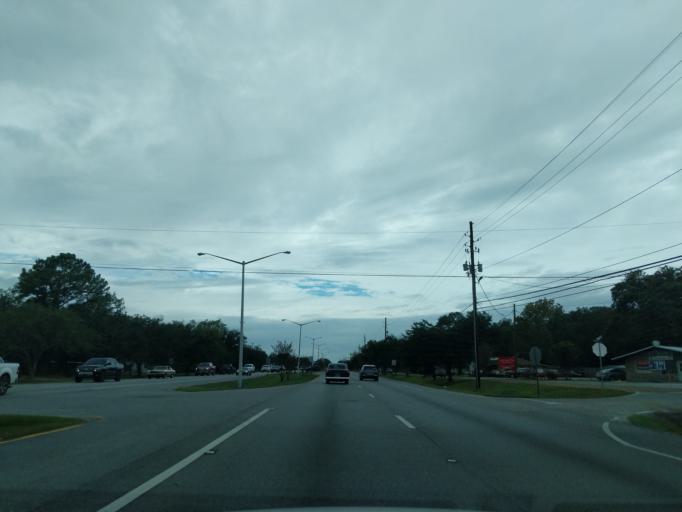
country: US
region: Mississippi
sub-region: Jackson County
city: Ocean Springs
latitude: 30.4164
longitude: -88.8112
